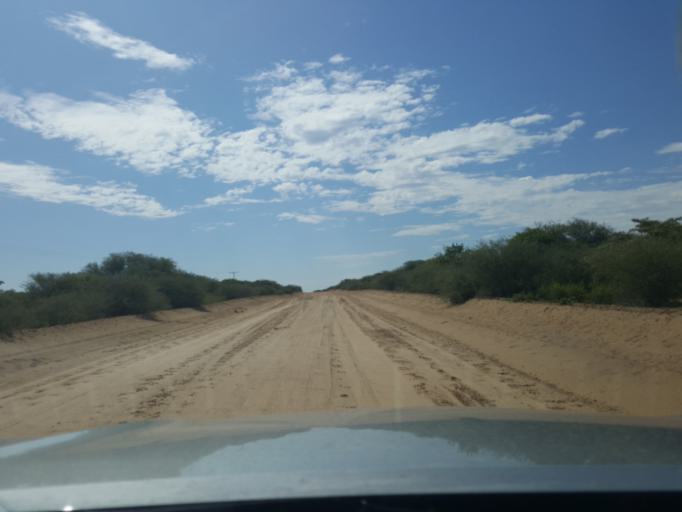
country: BW
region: Kweneng
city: Khudumelapye
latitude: -23.8719
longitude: 24.8979
